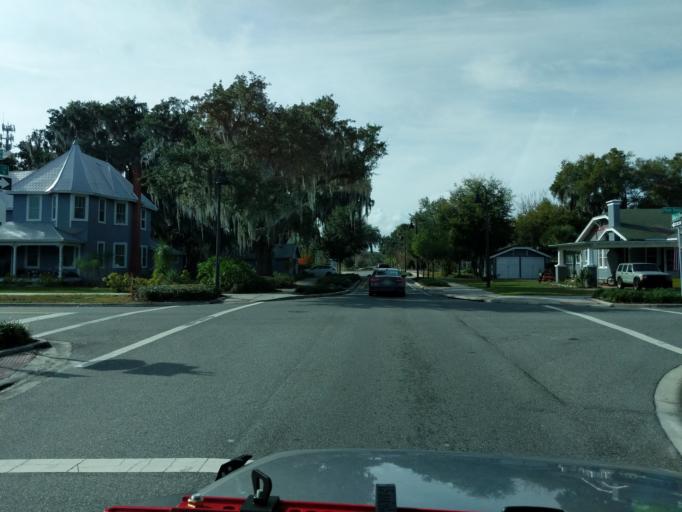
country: US
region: Florida
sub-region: Lake County
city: Tavares
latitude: 28.8051
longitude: -81.7278
